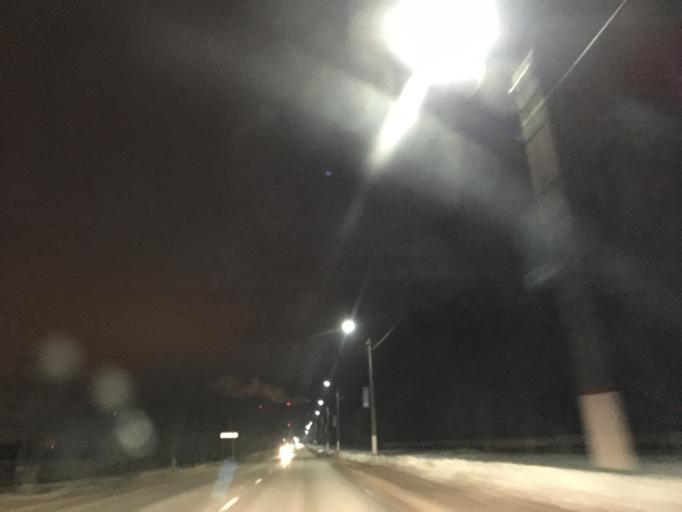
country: RU
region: Tula
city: Pervomayskiy
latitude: 54.0373
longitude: 37.5115
